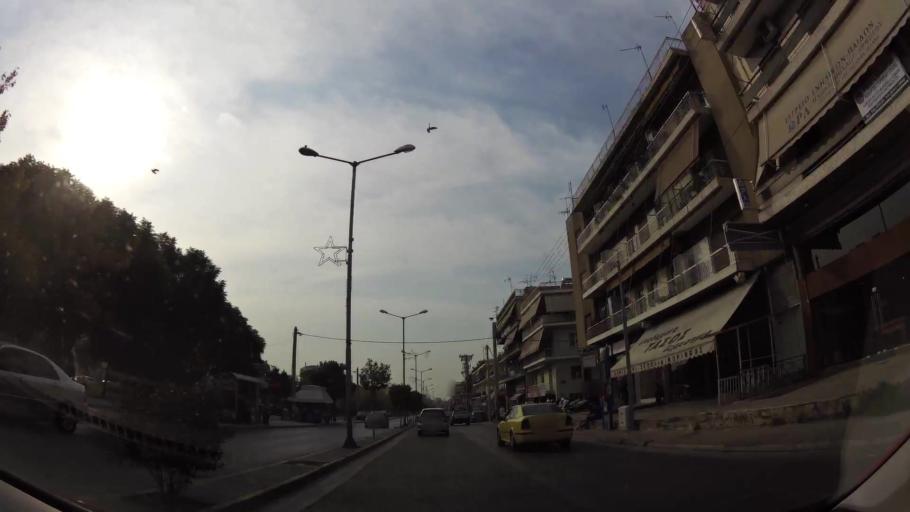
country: GR
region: Attica
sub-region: Nomarchia Athinas
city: Peristeri
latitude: 38.0112
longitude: 23.6882
